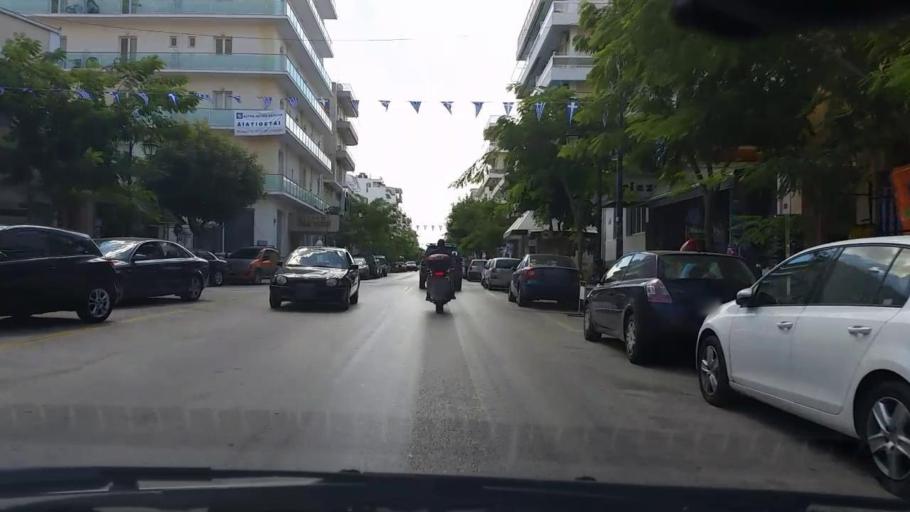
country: GR
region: Peloponnese
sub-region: Nomos Korinthias
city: Loutraki
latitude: 37.9780
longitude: 22.9772
